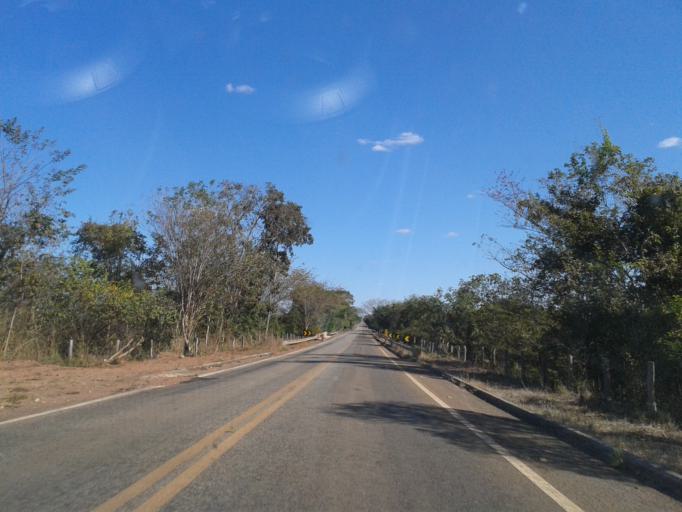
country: BR
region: Goias
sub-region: Mozarlandia
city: Mozarlandia
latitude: -14.5714
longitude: -50.5011
